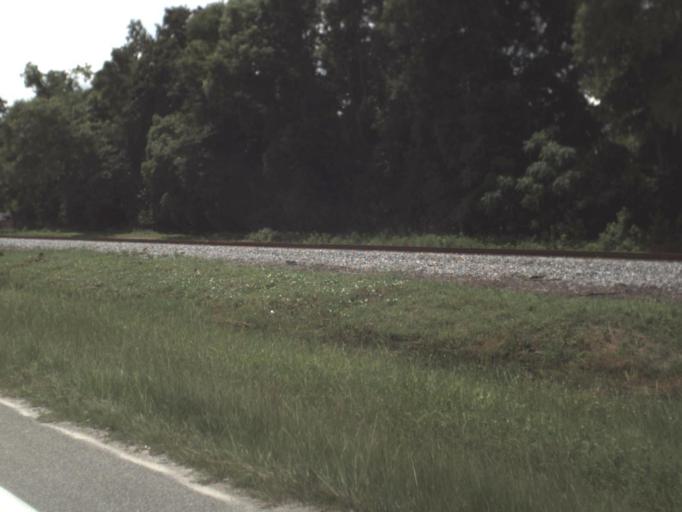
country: US
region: Florida
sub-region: Columbia County
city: Watertown
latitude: 30.1834
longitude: -82.5995
